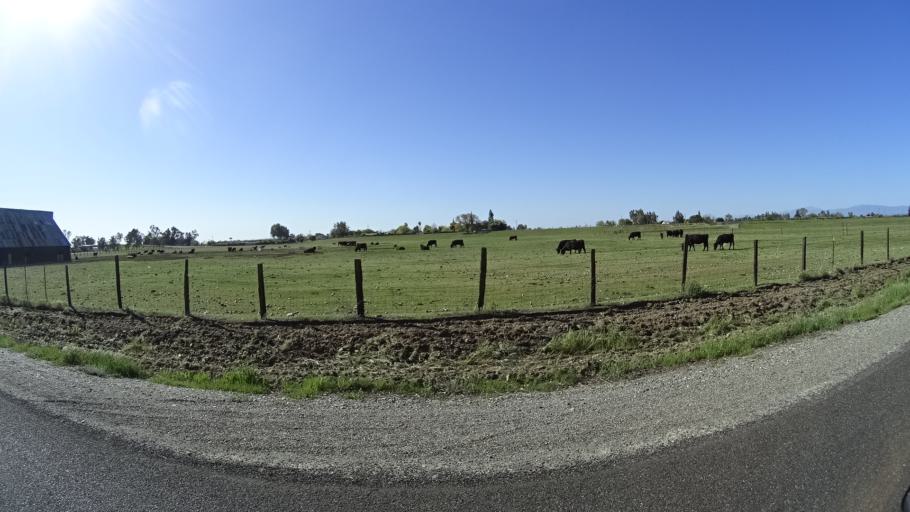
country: US
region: California
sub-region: Glenn County
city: Orland
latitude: 39.7440
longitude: -122.2103
